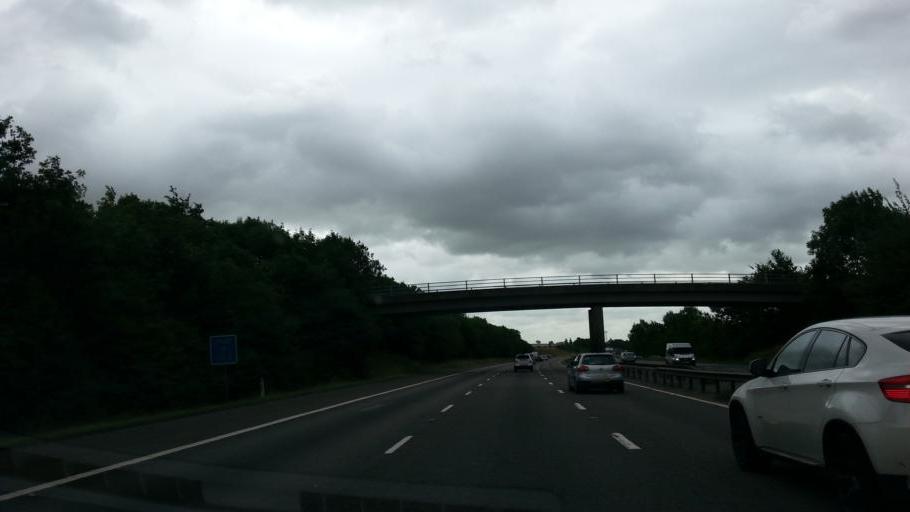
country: GB
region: England
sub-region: Oxfordshire
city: Hanwell
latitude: 52.1300
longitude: -1.3903
